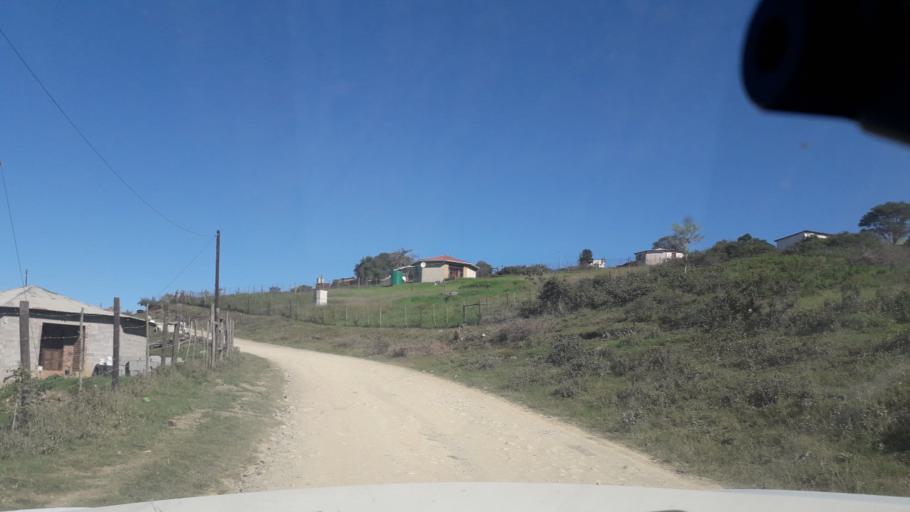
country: ZA
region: Eastern Cape
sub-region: Amathole District Municipality
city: Komga
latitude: -32.7660
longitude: 27.9483
